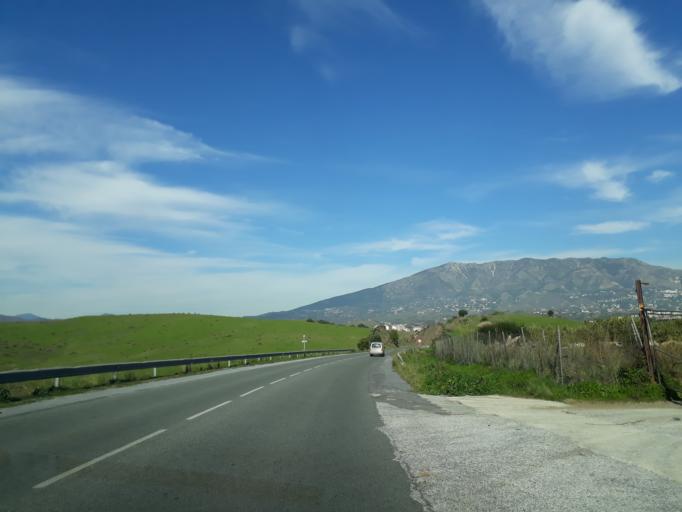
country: ES
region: Andalusia
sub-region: Provincia de Malaga
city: Fuengirola
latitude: 36.5331
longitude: -4.6860
